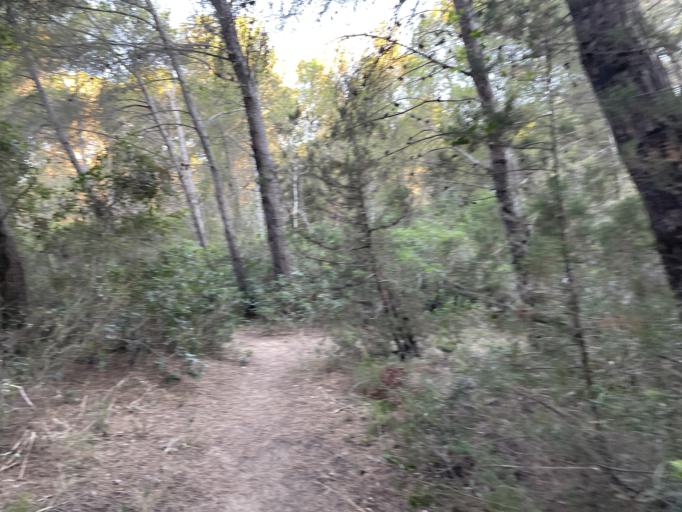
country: ES
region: Balearic Islands
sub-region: Illes Balears
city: Capdepera
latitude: 39.7179
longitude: 3.4550
